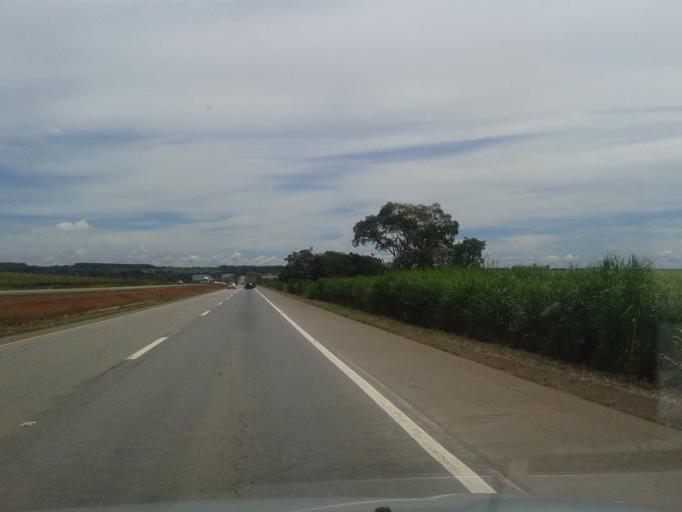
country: BR
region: Goias
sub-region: Hidrolandia
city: Hidrolandia
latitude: -17.0334
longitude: -49.2236
